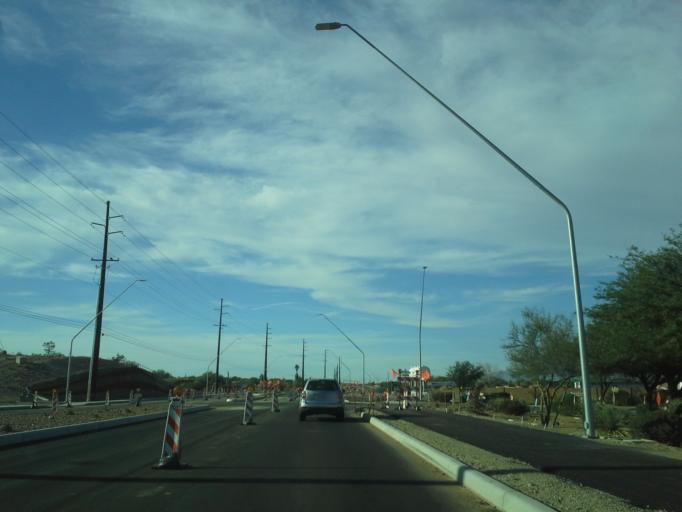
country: US
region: Arizona
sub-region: Pima County
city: Flowing Wells
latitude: 32.2554
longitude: -111.0163
